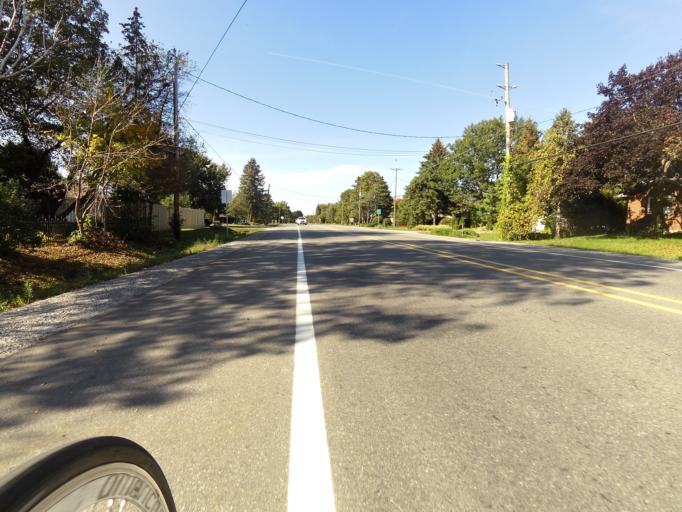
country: CA
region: Ontario
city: Bells Corners
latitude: 45.2520
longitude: -75.6967
